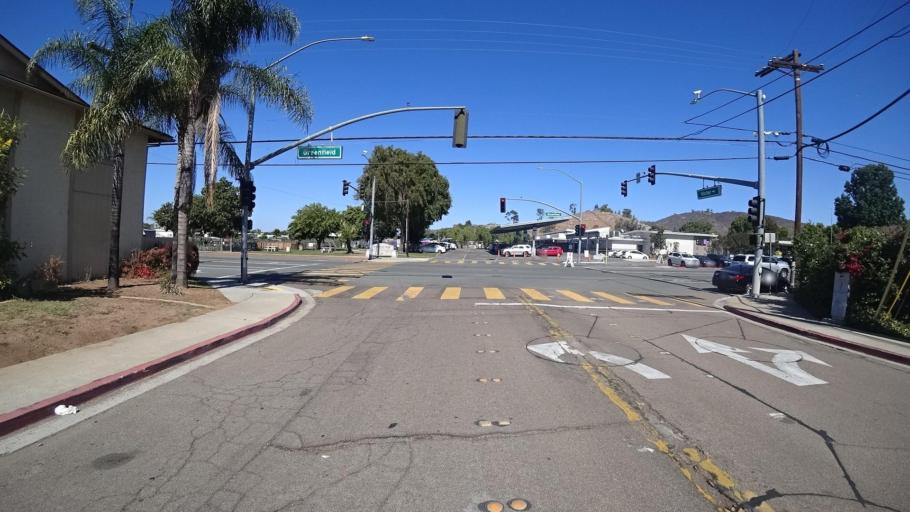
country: US
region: California
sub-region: San Diego County
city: El Cajon
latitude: 32.8131
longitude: -116.9553
